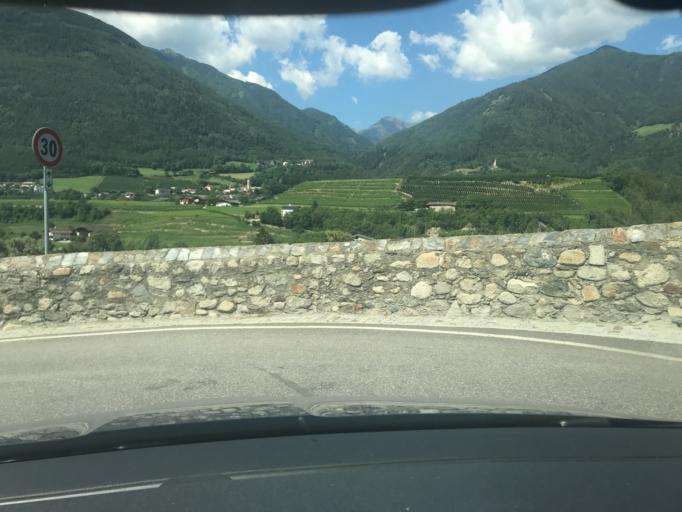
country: IT
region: Trentino-Alto Adige
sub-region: Bolzano
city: Leone-Santa Elisabetta
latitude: 46.7419
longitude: 11.6516
